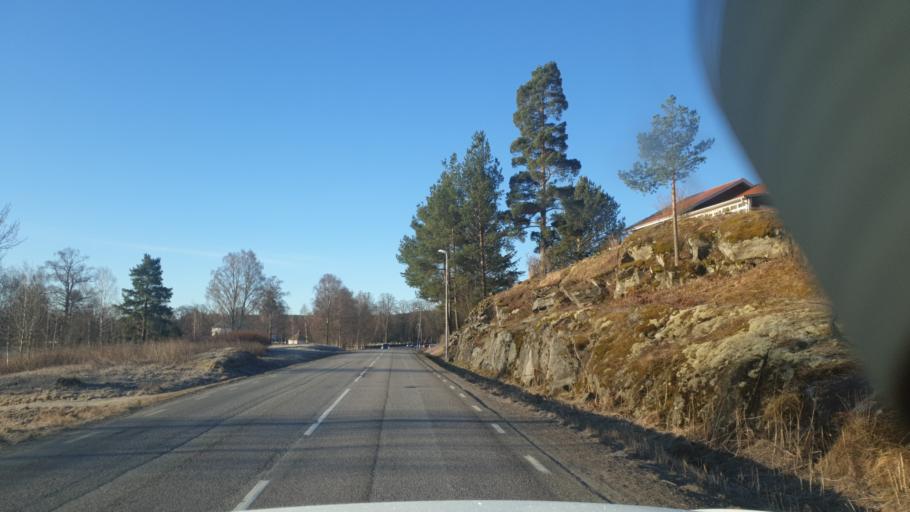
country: SE
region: Vaermland
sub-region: Eda Kommun
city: Charlottenberg
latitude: 59.8059
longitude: 12.2456
